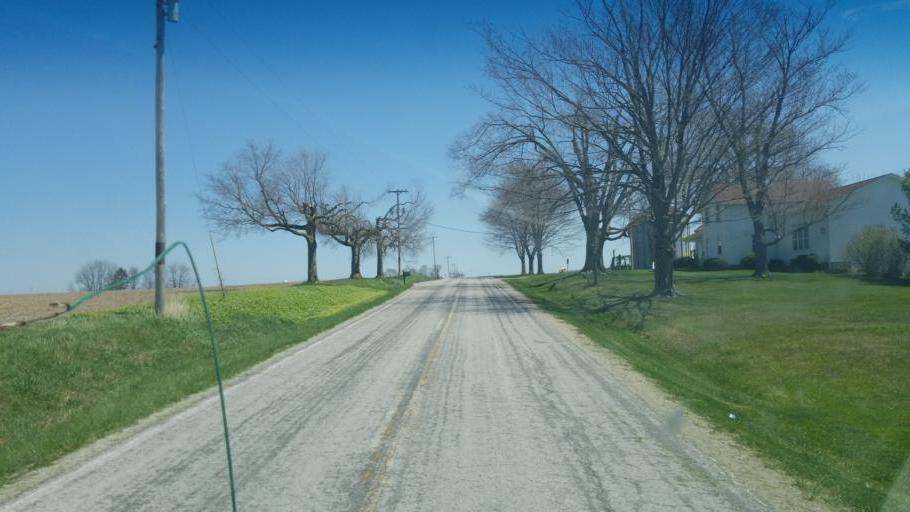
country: US
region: Ohio
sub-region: Huron County
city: New London
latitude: 41.1019
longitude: -82.3527
